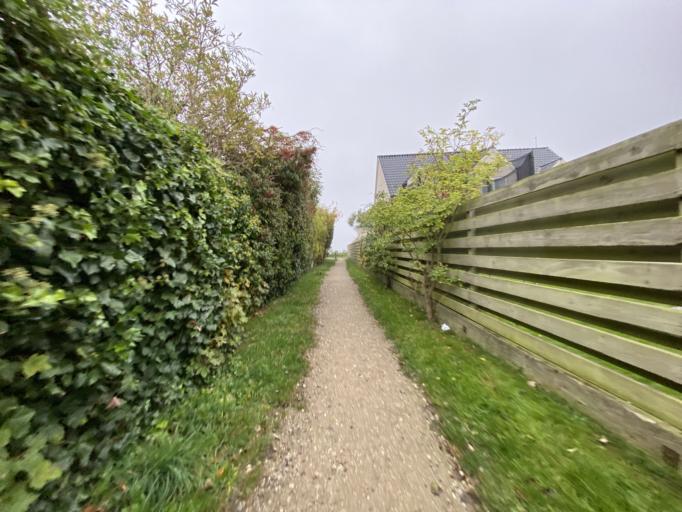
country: DK
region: Capital Region
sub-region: Dragor Kommune
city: Dragor
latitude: 55.6028
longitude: 12.6697
